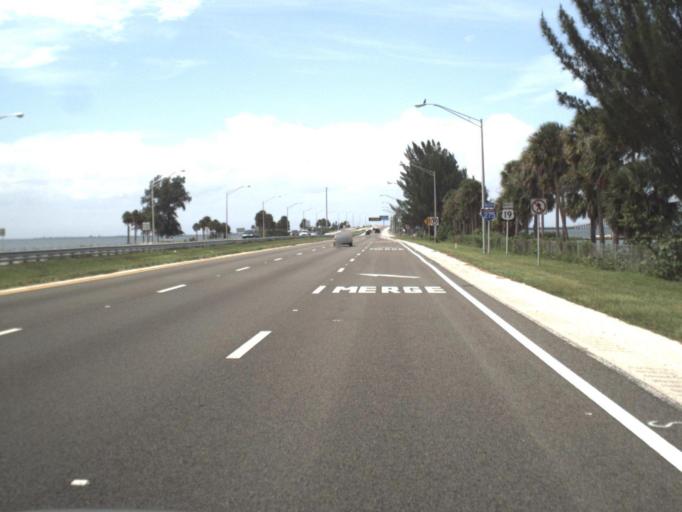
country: US
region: Florida
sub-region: Manatee County
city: Memphis
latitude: 27.5881
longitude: -82.6224
